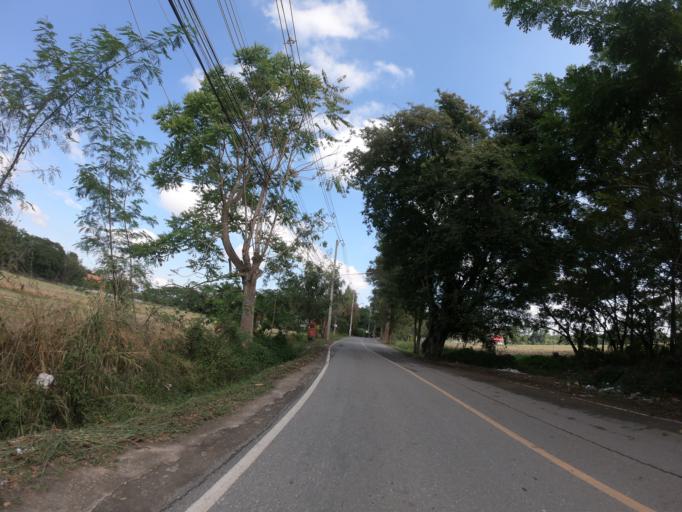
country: TH
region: Chiang Mai
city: San Sai
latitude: 18.8500
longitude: 99.0457
